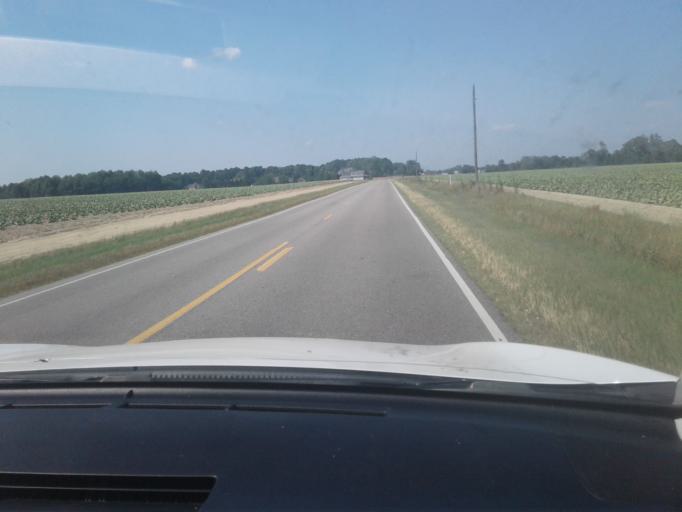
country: US
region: North Carolina
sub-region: Harnett County
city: Erwin
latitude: 35.3568
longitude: -78.6374
